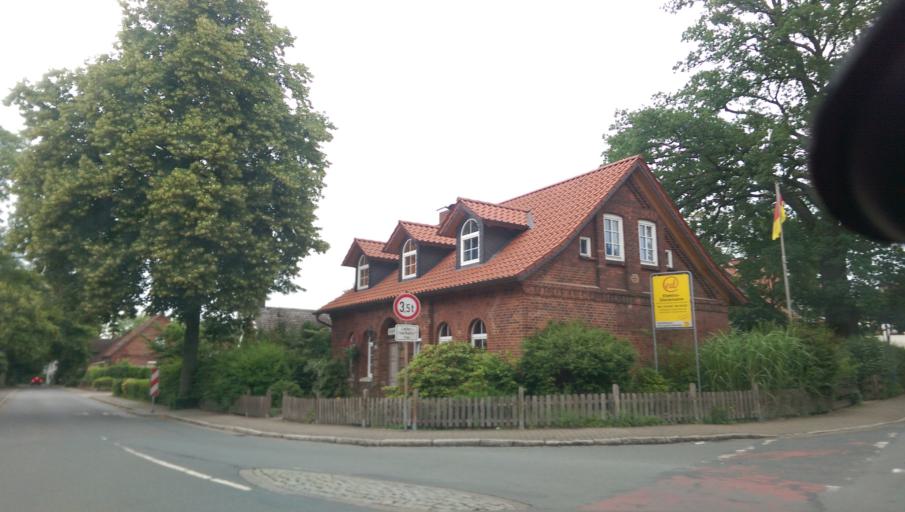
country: DE
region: Lower Saxony
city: Bad Fallingbostel
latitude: 52.8627
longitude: 9.6954
